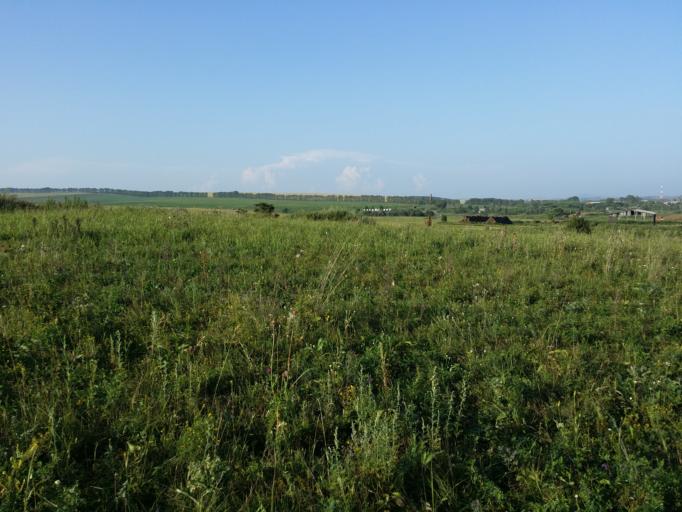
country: RU
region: Altai Krai
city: Verkh-Bekhtemir
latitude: 52.7619
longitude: 85.8820
